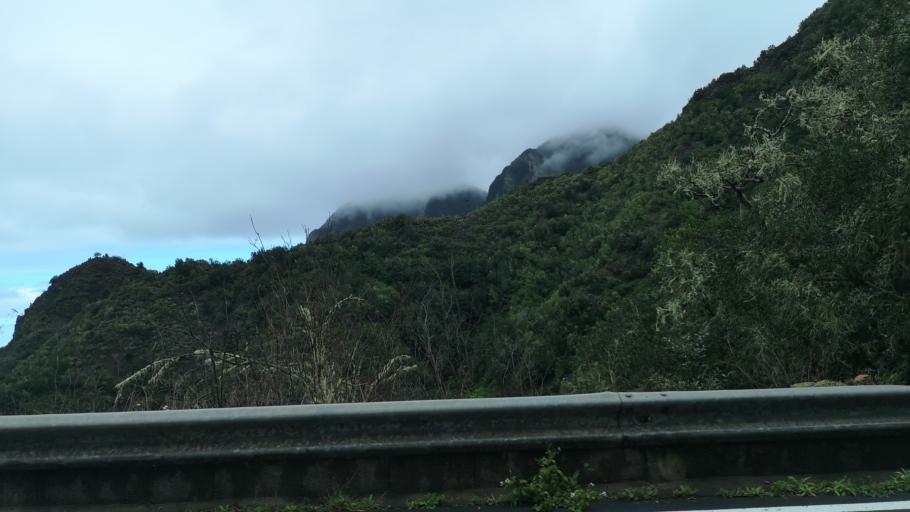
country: ES
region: Canary Islands
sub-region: Provincia de Santa Cruz de Tenerife
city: Hermigua
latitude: 28.1318
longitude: -17.2009
